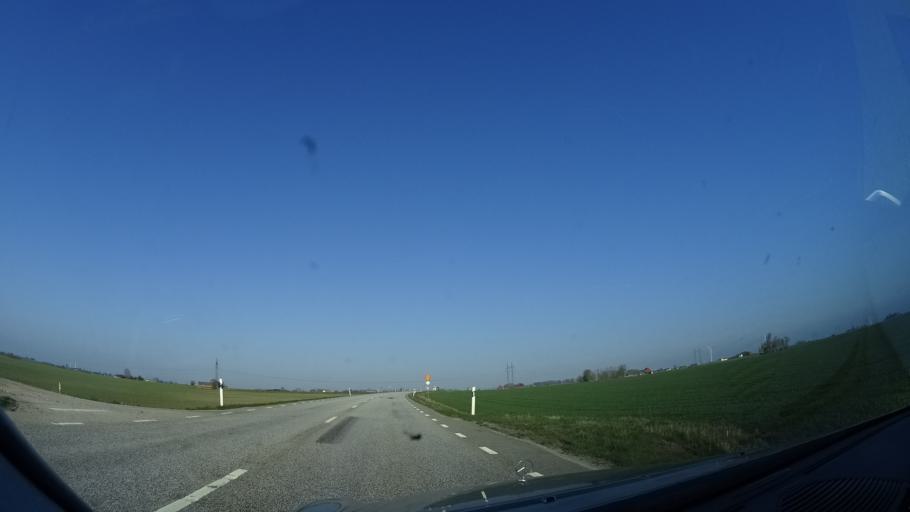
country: SE
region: Skane
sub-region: Svalovs Kommun
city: Teckomatorp
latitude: 55.8763
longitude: 13.0576
